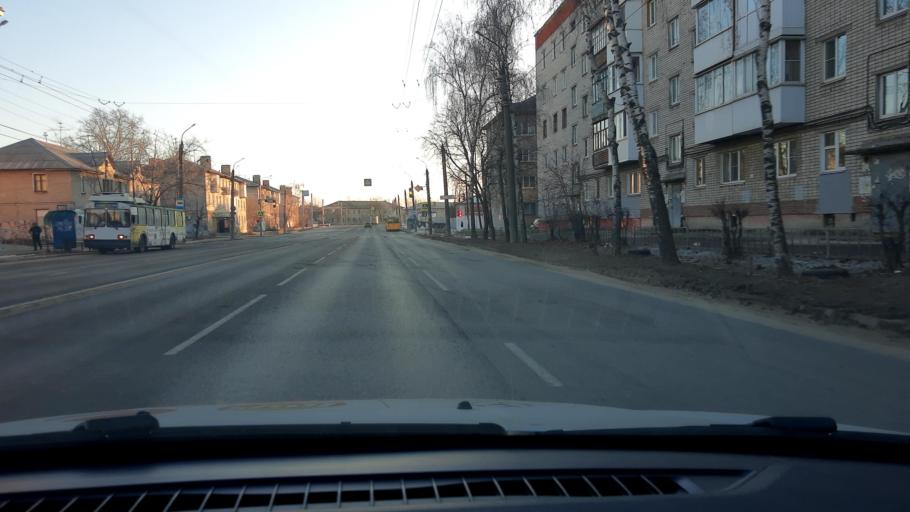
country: RU
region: Nizjnij Novgorod
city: Dzerzhinsk
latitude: 56.2476
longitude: 43.4708
